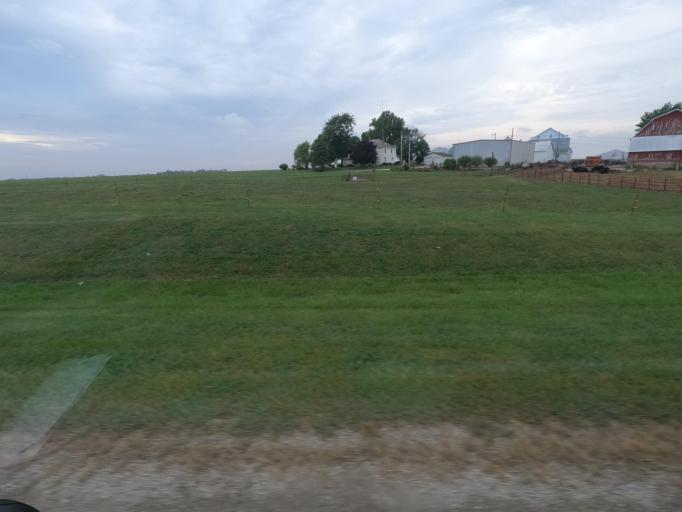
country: US
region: Iowa
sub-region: Henry County
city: Mount Pleasant
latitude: 40.8124
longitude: -91.7044
